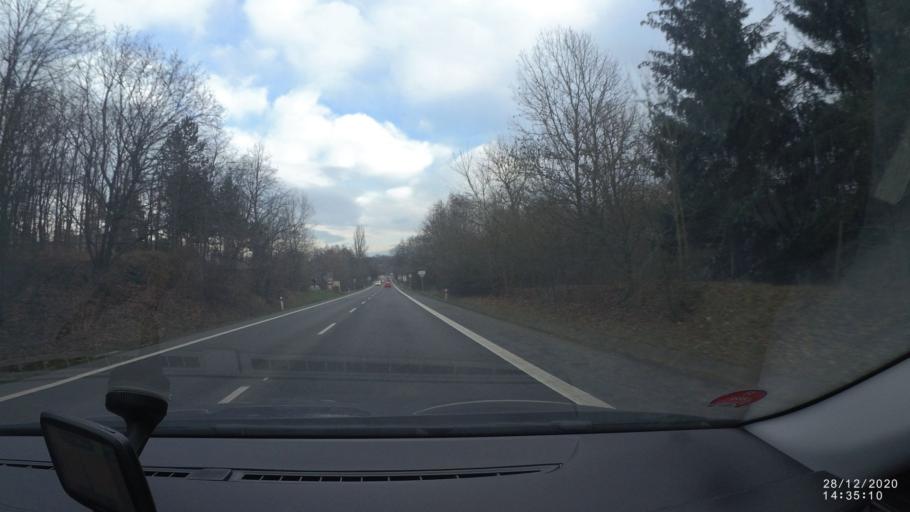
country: CZ
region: Central Bohemia
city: Uvaly
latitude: 50.0695
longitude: 14.7166
